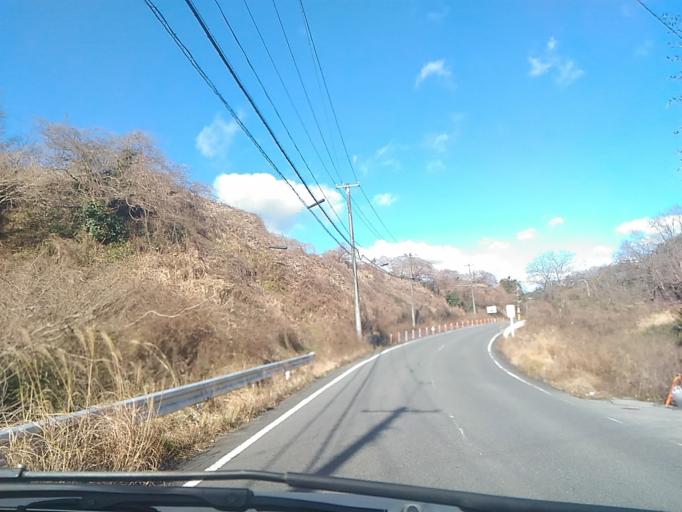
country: JP
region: Fukushima
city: Iwaki
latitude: 37.0031
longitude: 140.8171
